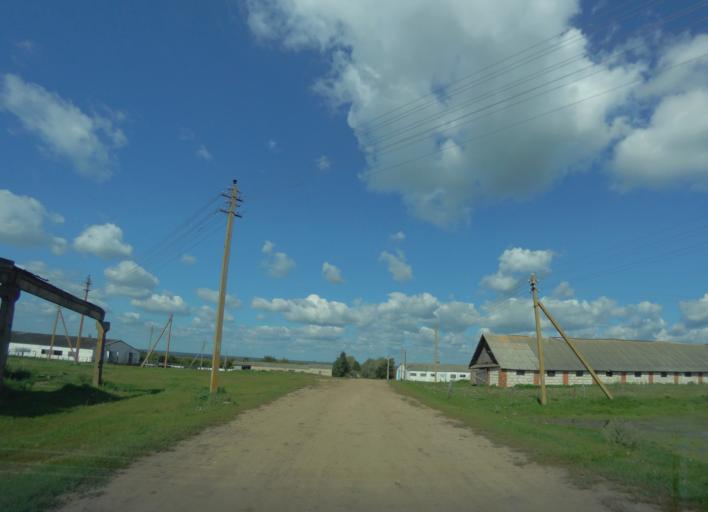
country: BY
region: Minsk
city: Zyembin
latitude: 54.4106
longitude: 28.3836
